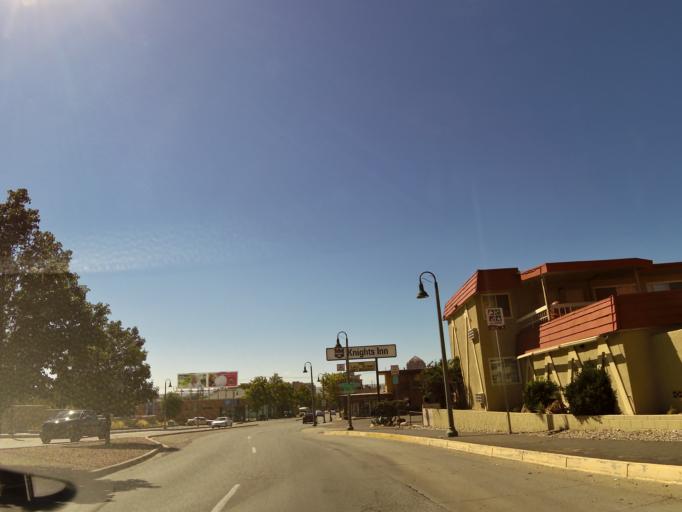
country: US
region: New Mexico
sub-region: Bernalillo County
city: Albuquerque
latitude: 35.0829
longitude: -106.6376
